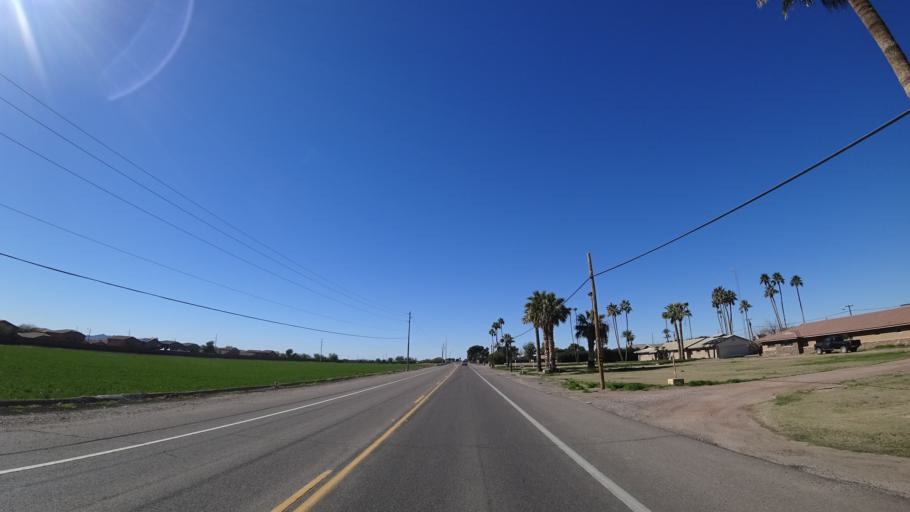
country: US
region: Arizona
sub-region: Maricopa County
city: Buckeye
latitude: 33.3704
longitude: -112.5957
